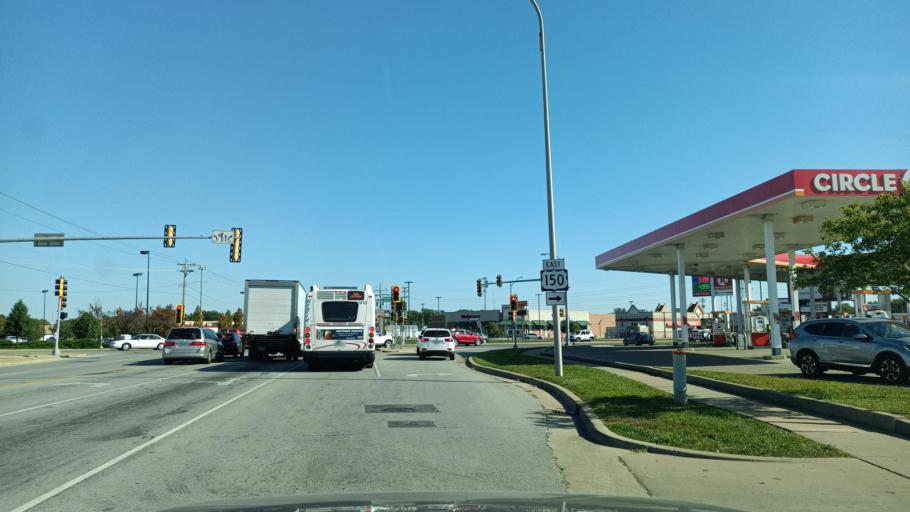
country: US
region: Illinois
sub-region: Champaign County
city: Champaign
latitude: 40.1324
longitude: -88.2587
